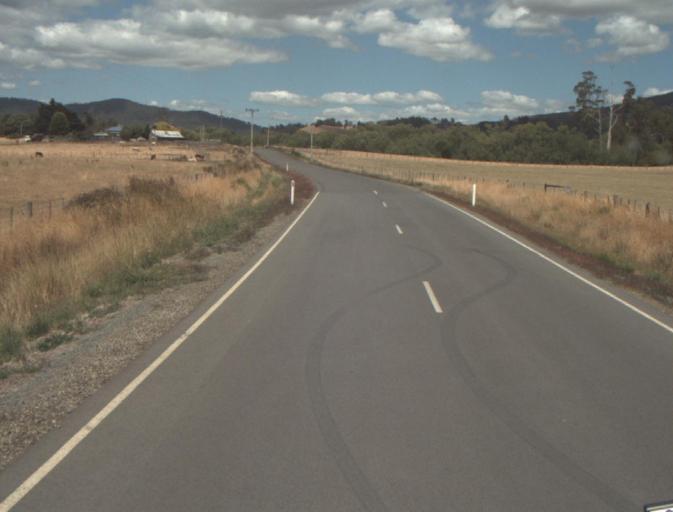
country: AU
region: Tasmania
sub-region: Launceston
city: Mayfield
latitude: -41.2211
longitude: 147.1373
